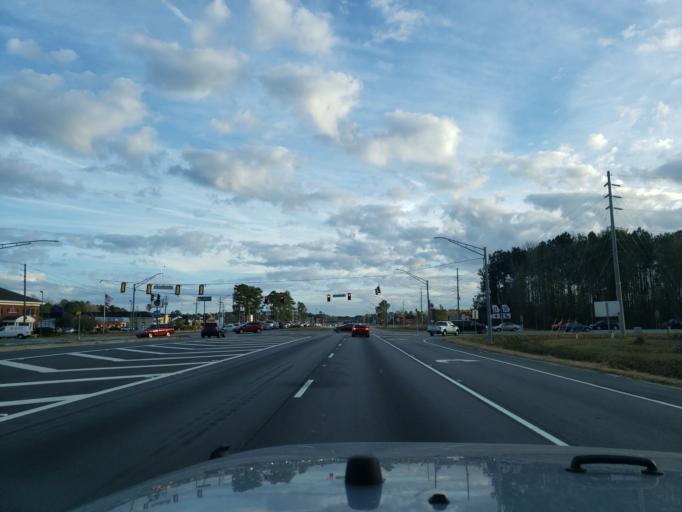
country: US
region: Georgia
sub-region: Chatham County
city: Port Wentworth
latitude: 32.1992
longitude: -81.1980
